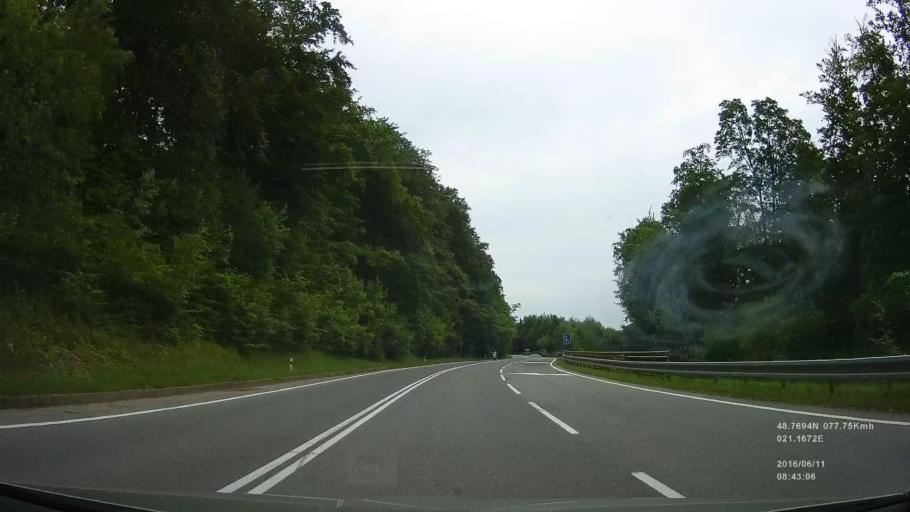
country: SK
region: Kosicky
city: Kosice
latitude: 48.7656
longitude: 21.1661
